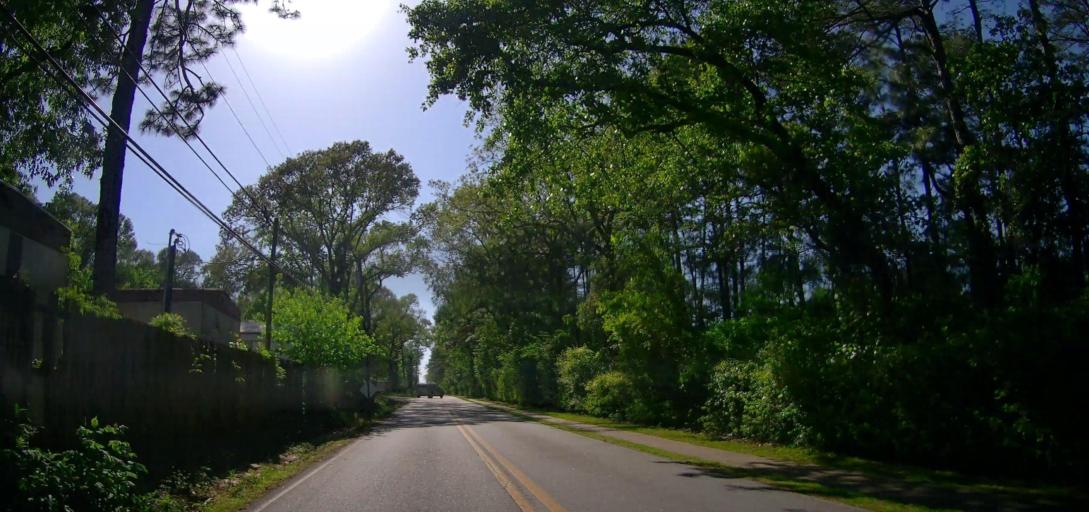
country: US
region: Georgia
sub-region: Houston County
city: Warner Robins
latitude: 32.6017
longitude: -83.6046
